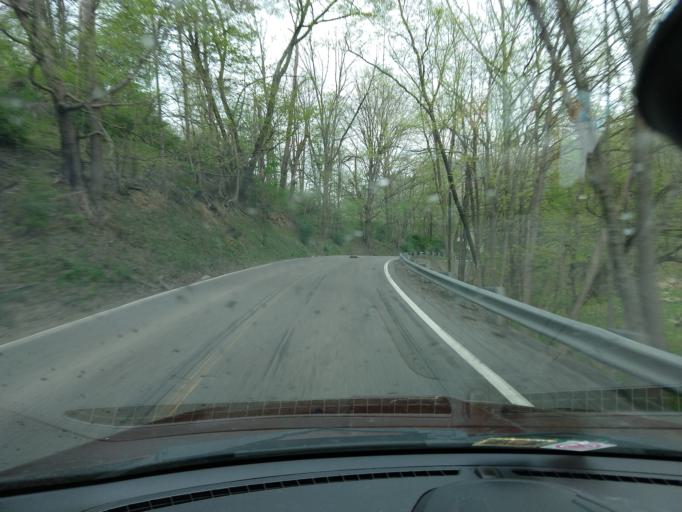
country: US
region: West Virginia
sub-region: Harrison County
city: Despard
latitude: 39.3301
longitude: -80.2895
